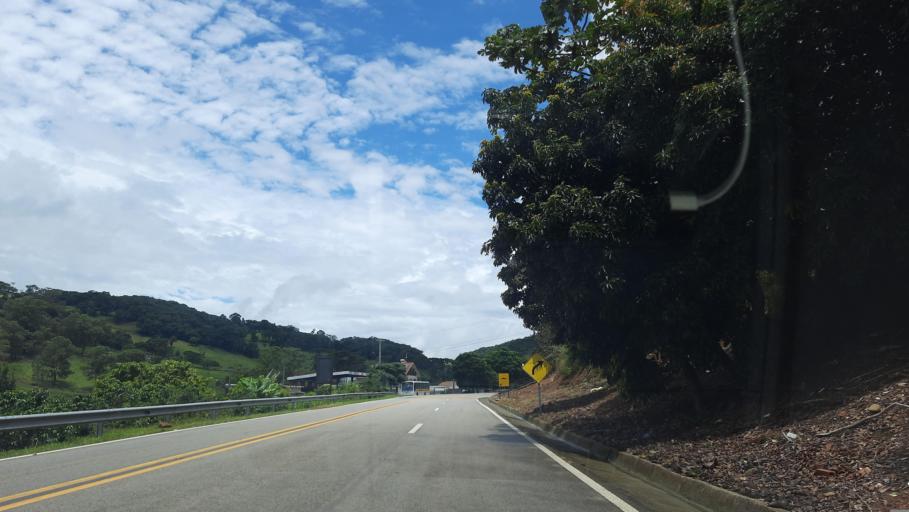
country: BR
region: Sao Paulo
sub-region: Sao Joao Da Boa Vista
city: Sao Joao da Boa Vista
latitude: -21.8354
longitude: -46.7458
